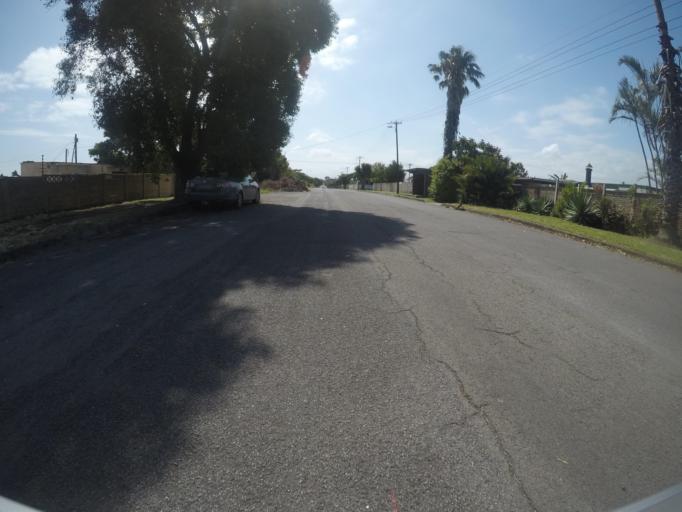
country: ZA
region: Eastern Cape
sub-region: Buffalo City Metropolitan Municipality
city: East London
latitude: -32.9792
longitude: 27.8746
